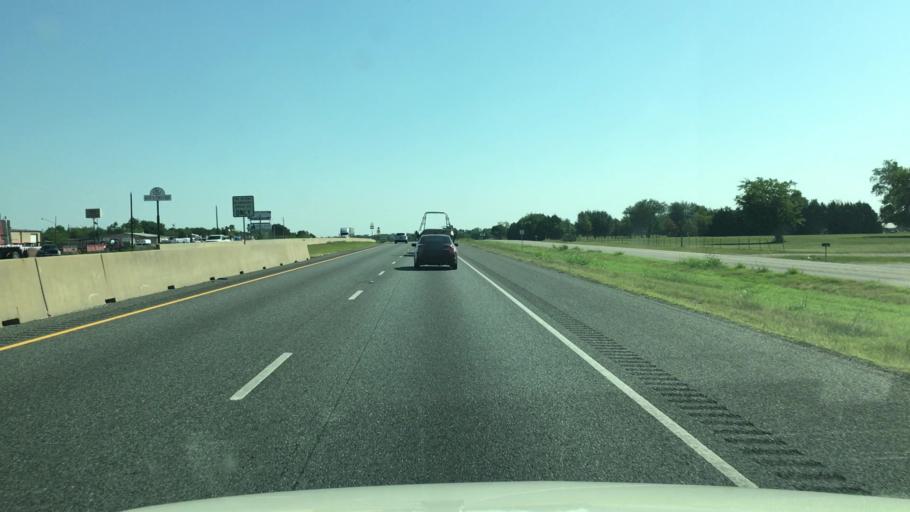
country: US
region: Texas
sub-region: Hunt County
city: Caddo Mills
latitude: 33.0314
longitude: -96.1899
